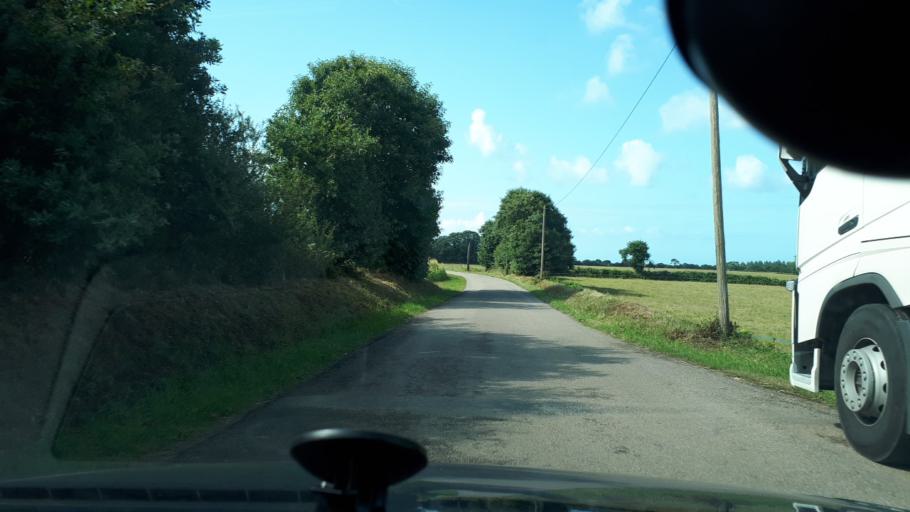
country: FR
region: Brittany
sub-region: Departement du Finistere
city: Pouldreuzic
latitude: 47.9841
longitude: -4.3687
